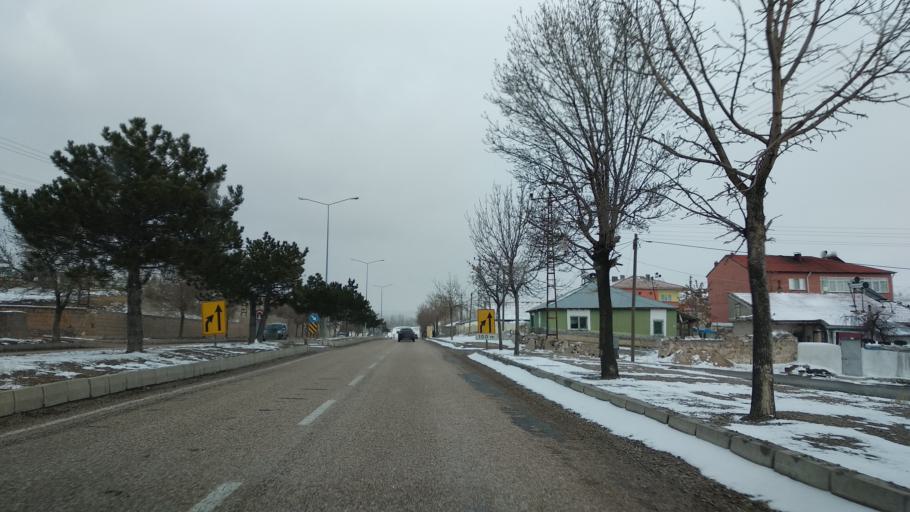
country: TR
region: Kayseri
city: Pinarbasi
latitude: 38.7252
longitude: 36.3945
